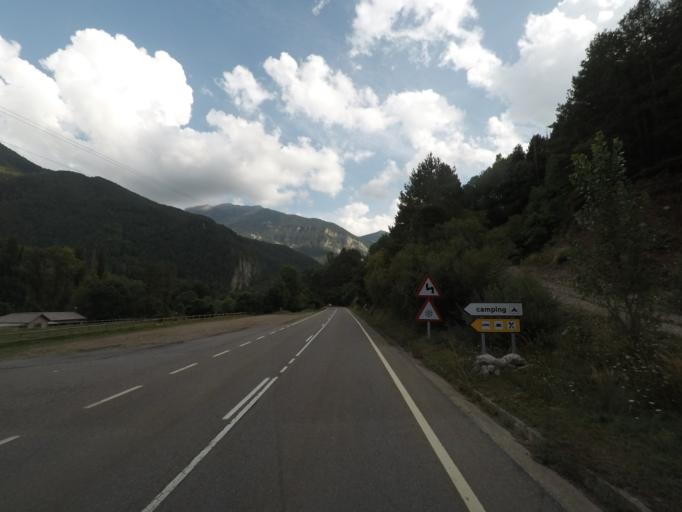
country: ES
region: Aragon
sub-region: Provincia de Huesca
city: Bielsa
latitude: 42.6288
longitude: 0.2243
